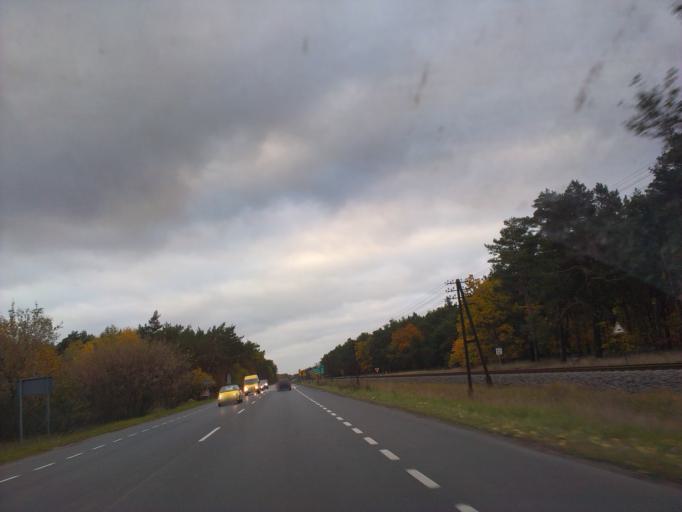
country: PL
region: Kujawsko-Pomorskie
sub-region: Powiat torunski
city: Lysomice
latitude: 53.0565
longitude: 18.6177
